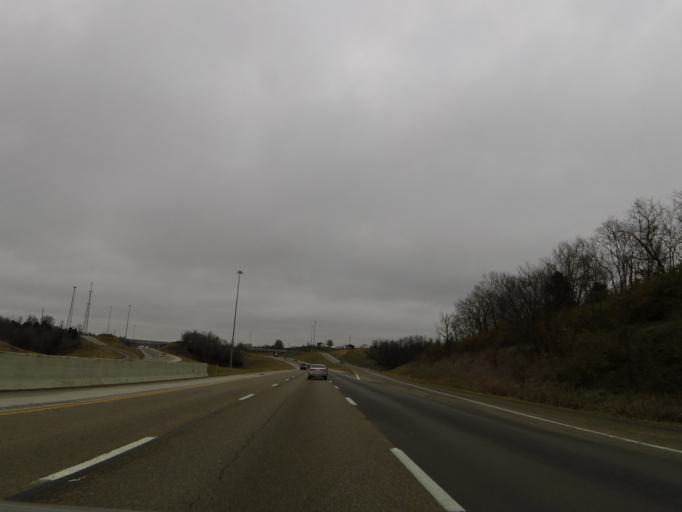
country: US
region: Kentucky
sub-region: Grant County
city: Dry Ridge
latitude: 38.6530
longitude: -84.5875
